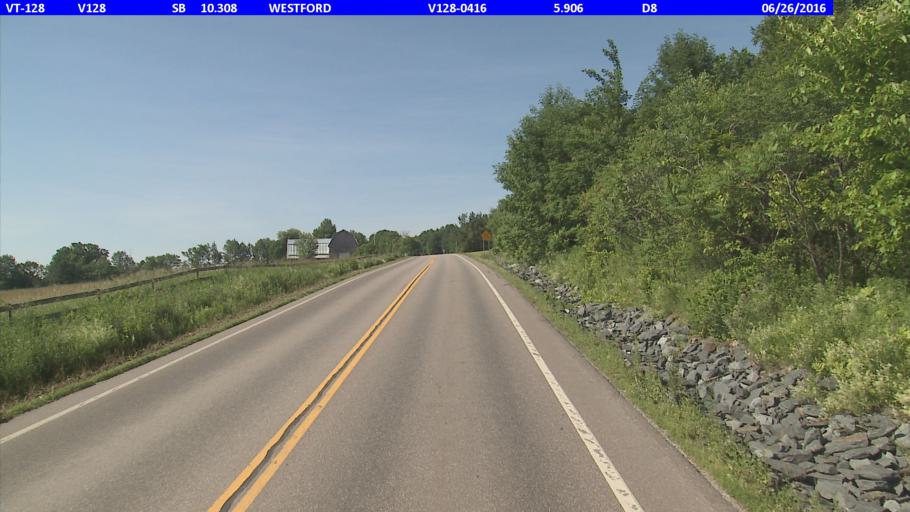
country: US
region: Vermont
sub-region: Chittenden County
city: Milton
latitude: 44.6382
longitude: -73.0167
